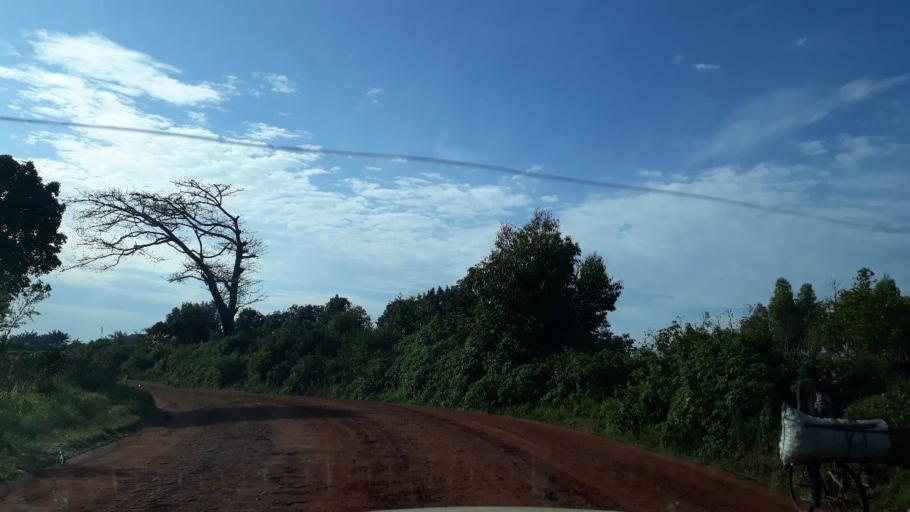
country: UG
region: Northern Region
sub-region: Zombo District
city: Paidha
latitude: 2.2508
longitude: 30.9009
